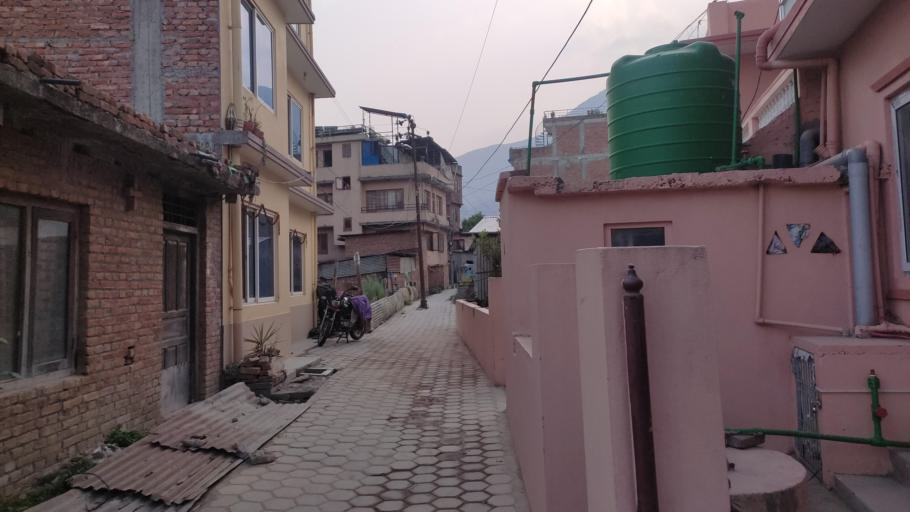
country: NP
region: Central Region
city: Kirtipur
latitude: 27.6689
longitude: 85.2736
